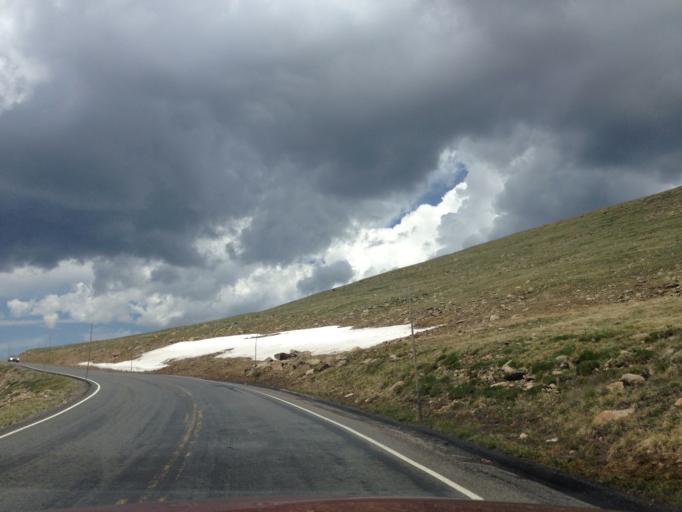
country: US
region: Colorado
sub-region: Larimer County
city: Estes Park
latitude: 40.4037
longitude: -105.7106
